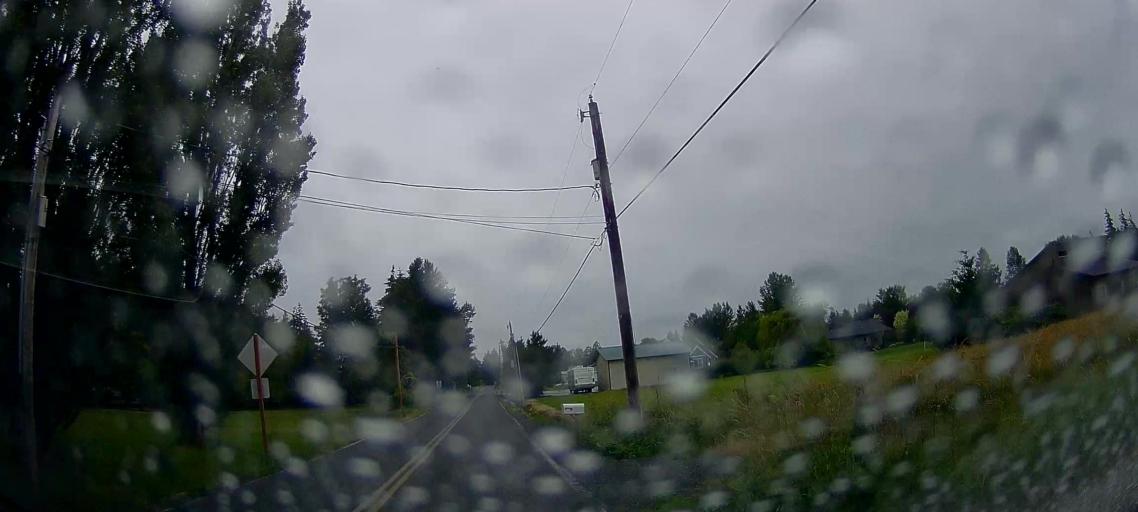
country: US
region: Washington
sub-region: Whatcom County
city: Marietta
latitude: 48.7978
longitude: -122.5762
